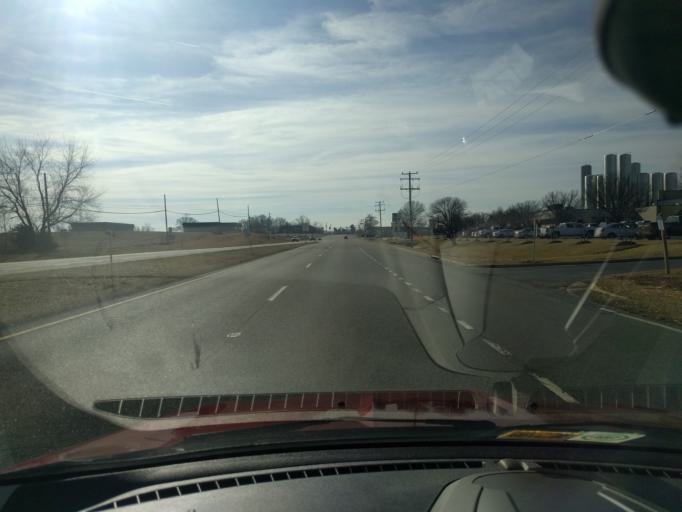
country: US
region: Virginia
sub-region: Rockingham County
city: Bridgewater
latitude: 38.3681
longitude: -78.9362
